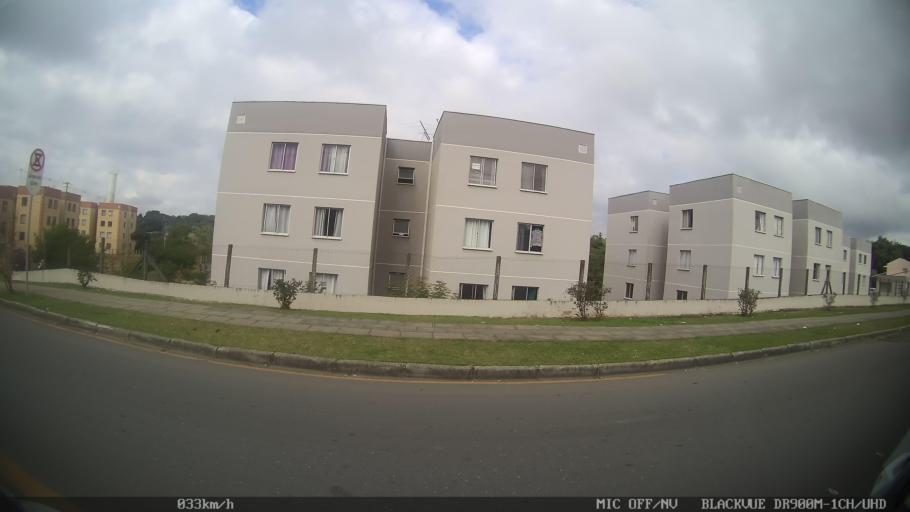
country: BR
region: Parana
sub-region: Almirante Tamandare
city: Almirante Tamandare
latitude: -25.3521
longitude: -49.2528
